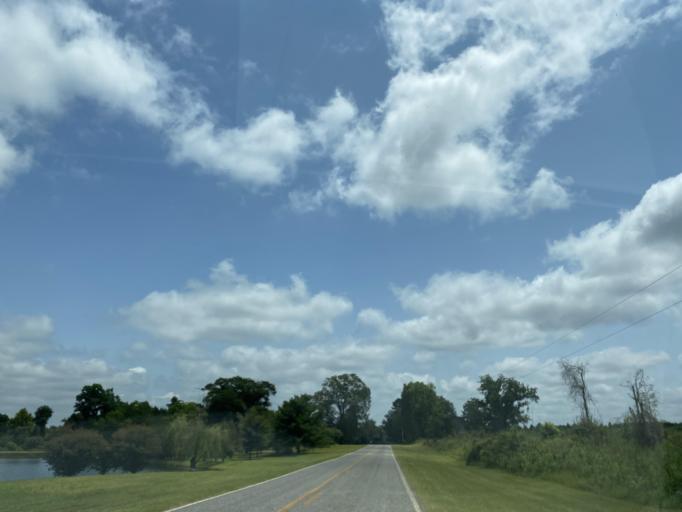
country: US
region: Georgia
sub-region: Wheeler County
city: Alamo
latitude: 32.0816
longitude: -82.7547
